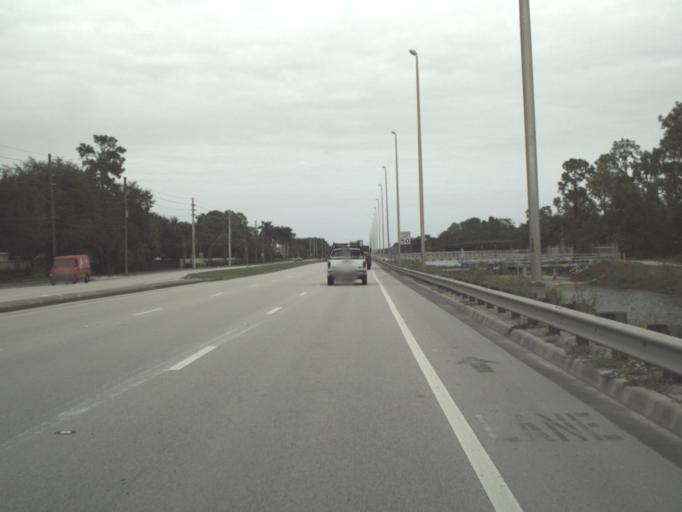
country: US
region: Florida
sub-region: Collier County
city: Golden Gate
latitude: 26.1379
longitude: -81.6867
